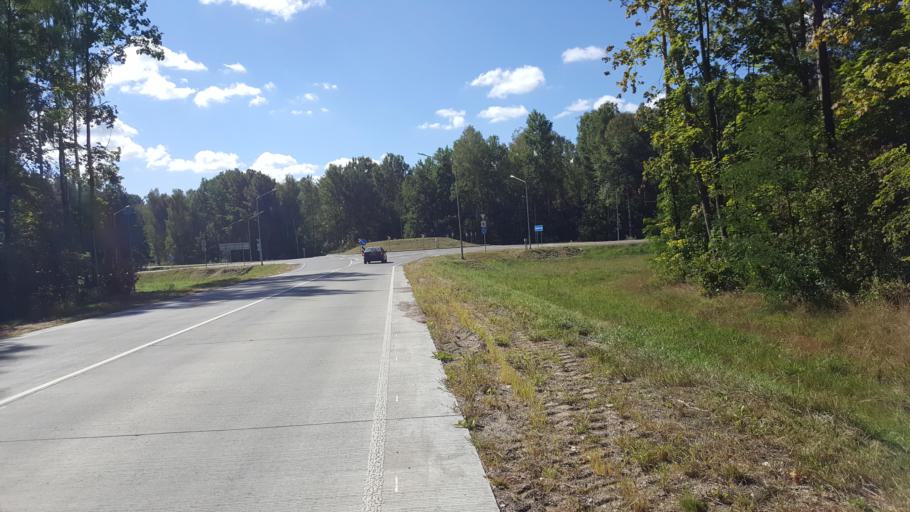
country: BY
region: Brest
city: Vysokaye
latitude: 52.3530
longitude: 23.4069
